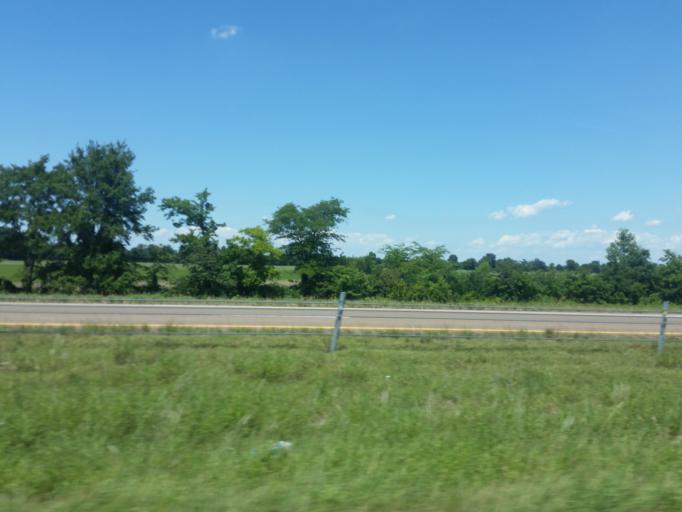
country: US
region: Missouri
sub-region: Pemiscot County
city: Caruthersville
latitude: 36.0919
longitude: -89.5806
